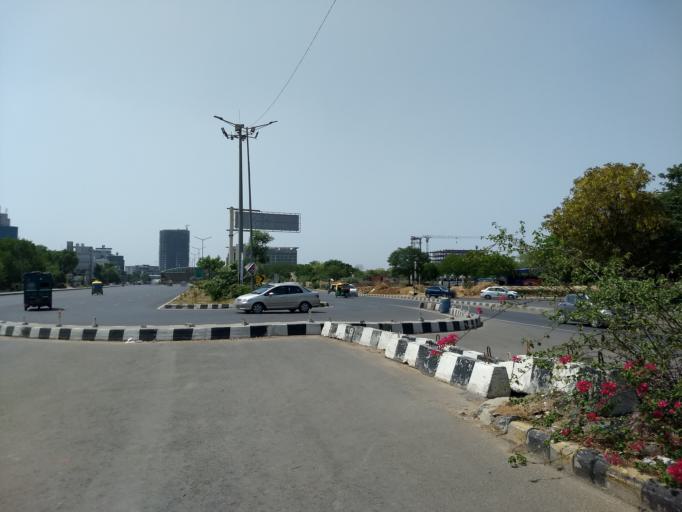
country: IN
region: Haryana
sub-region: Gurgaon
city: Gurgaon
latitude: 28.4644
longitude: 77.0635
